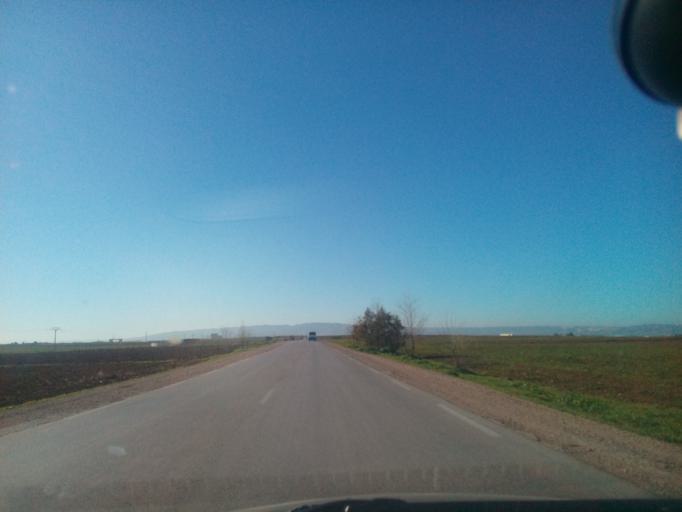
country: DZ
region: Relizane
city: Djidiouia
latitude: 35.8944
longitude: 0.6518
